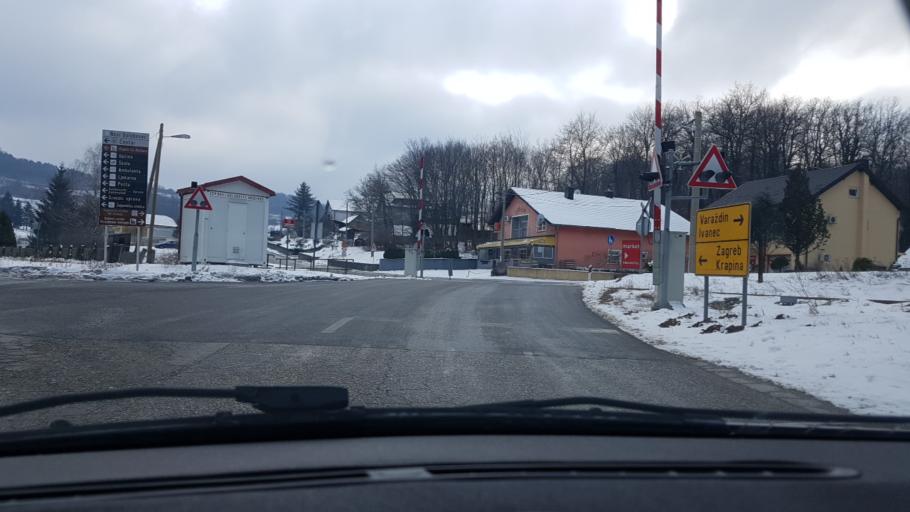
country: HR
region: Krapinsko-Zagorska
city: Mihovljan
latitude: 46.1750
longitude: 15.9831
